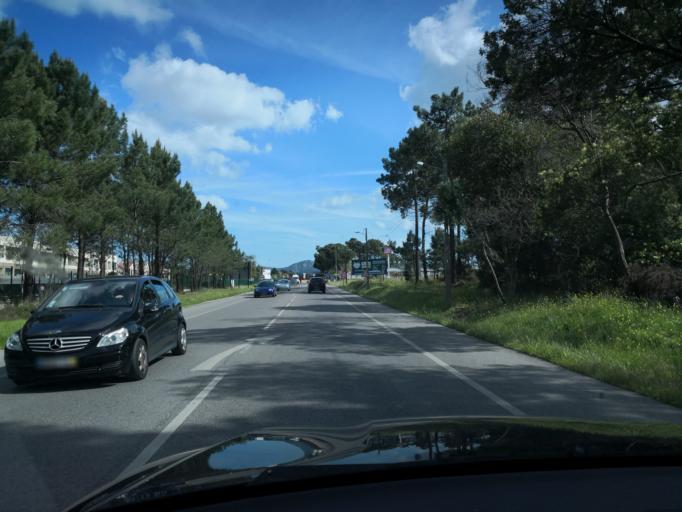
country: PT
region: Setubal
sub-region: Barreiro
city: Santo Antonio da Charneca
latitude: 38.5470
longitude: -9.0305
